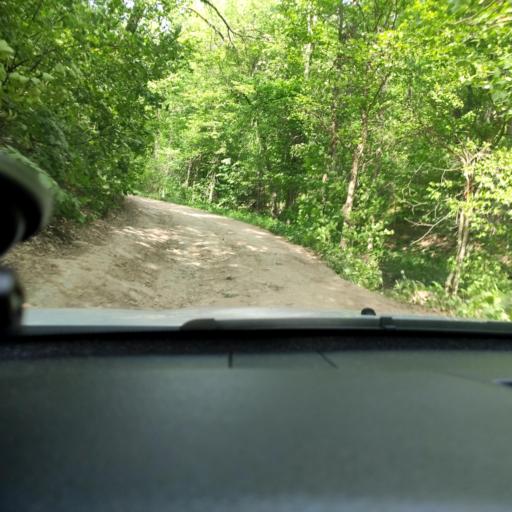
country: RU
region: Samara
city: Volzhskiy
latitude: 53.3375
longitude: 50.2172
